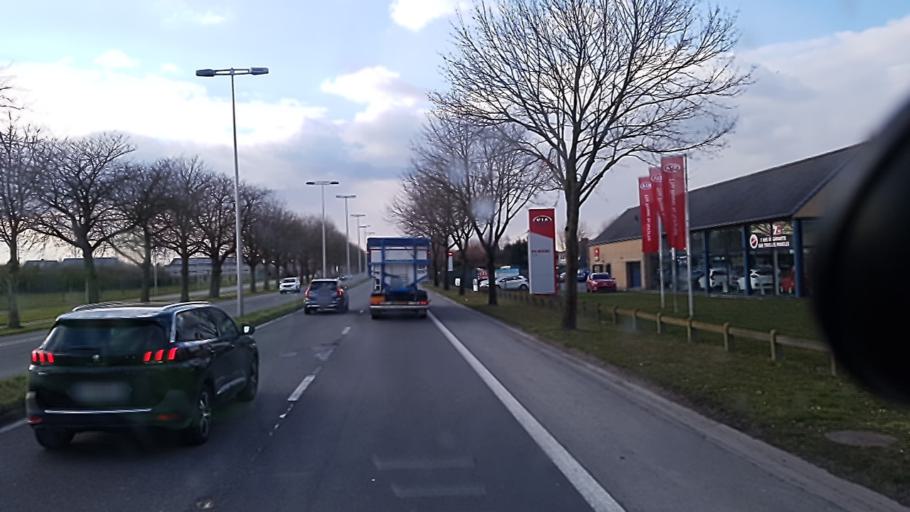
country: BE
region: Wallonia
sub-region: Province du Hainaut
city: Estaimpuis
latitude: 50.7338
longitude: 3.2823
